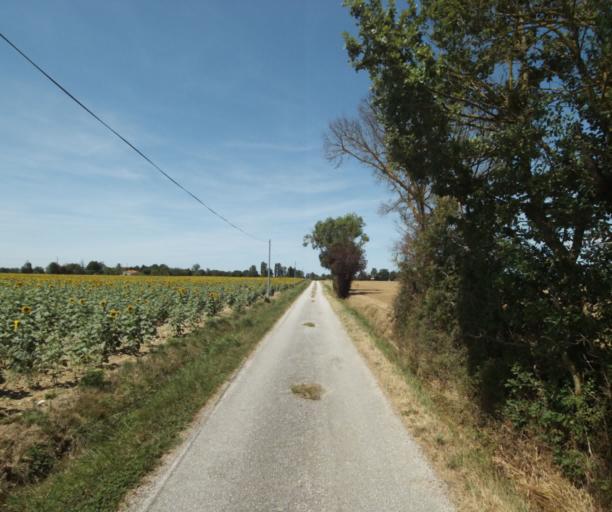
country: FR
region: Midi-Pyrenees
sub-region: Departement de la Haute-Garonne
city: Revel
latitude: 43.4996
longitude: 2.0286
